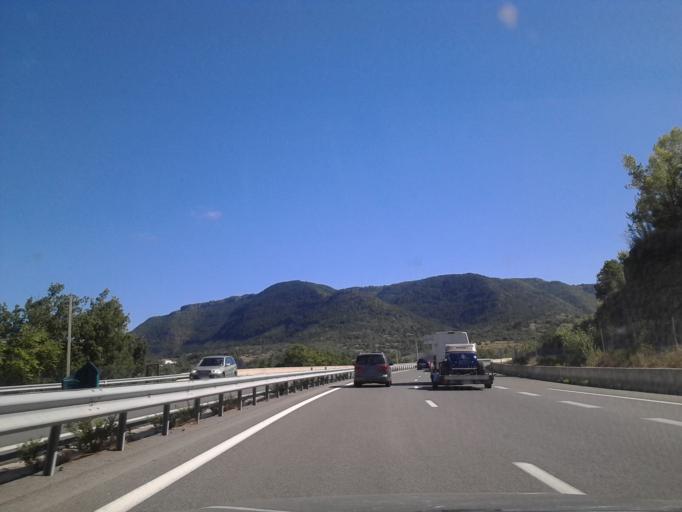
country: FR
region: Languedoc-Roussillon
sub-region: Departement de l'Herault
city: Lodeve
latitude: 43.7599
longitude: 3.3298
